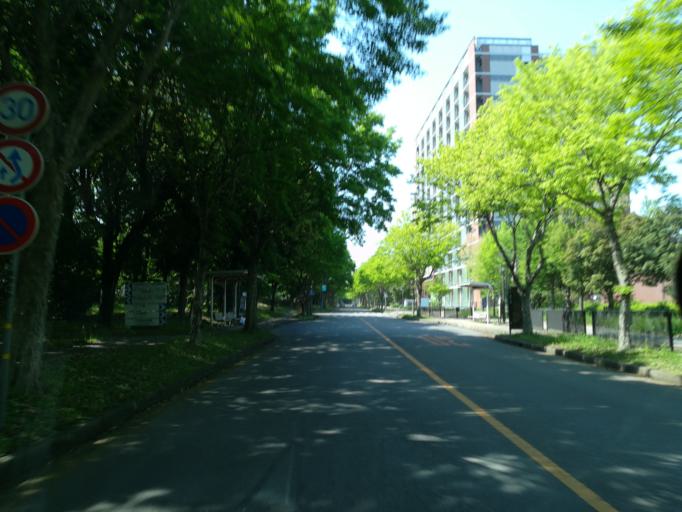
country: JP
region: Ibaraki
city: Naka
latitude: 36.1075
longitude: 140.1001
